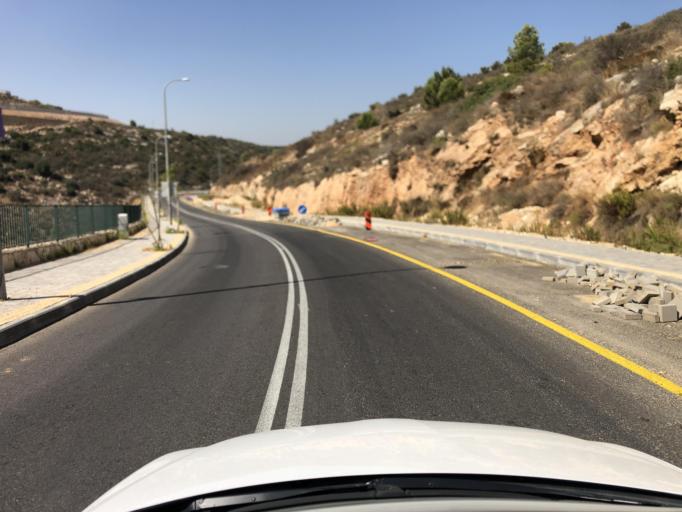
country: PS
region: West Bank
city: An Nabi Ilyas
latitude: 32.1653
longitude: 35.0159
